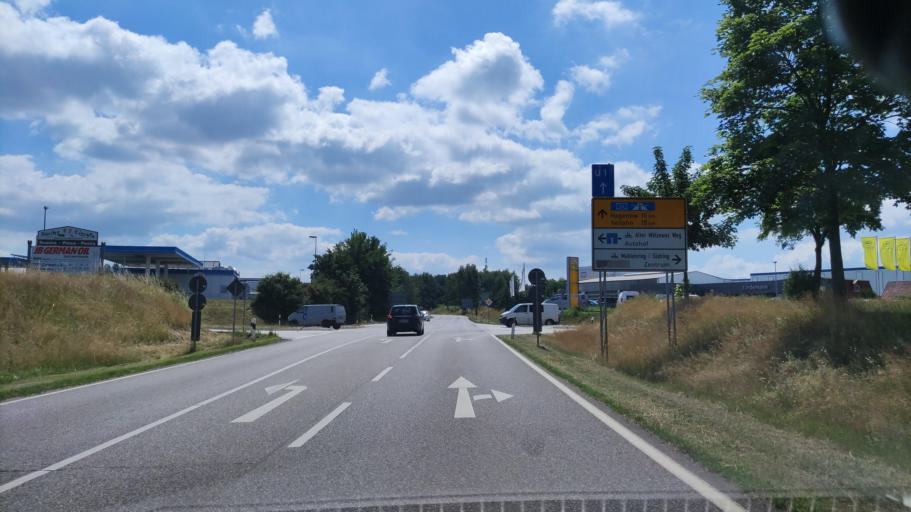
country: DE
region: Mecklenburg-Vorpommern
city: Wittenburg
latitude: 53.5031
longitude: 11.0976
